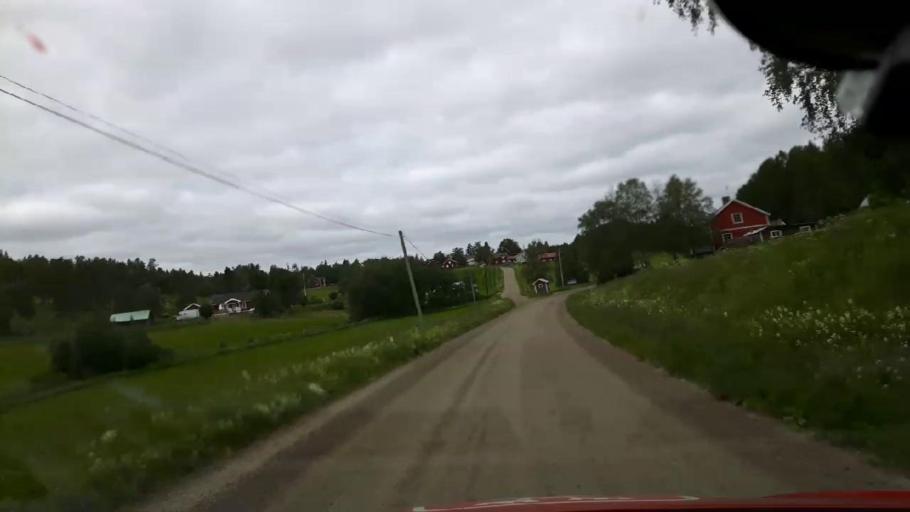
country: SE
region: Jaemtland
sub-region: OEstersunds Kommun
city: Brunflo
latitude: 62.9181
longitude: 15.0183
